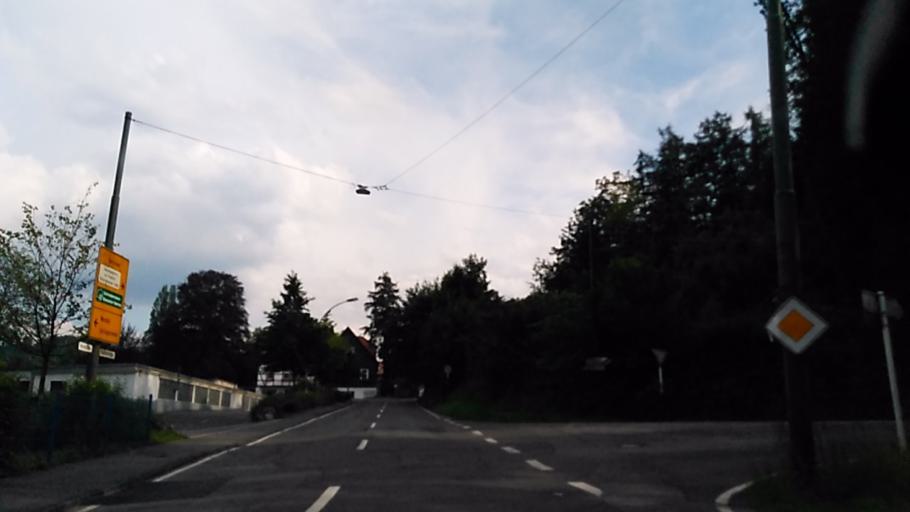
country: DE
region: North Rhine-Westphalia
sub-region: Regierungsbezirk Arnsberg
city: Herscheid
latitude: 51.2205
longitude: 7.6931
